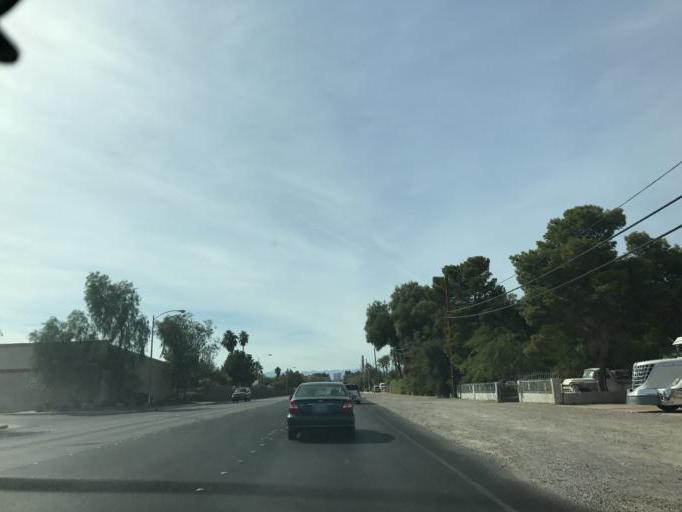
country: US
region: Nevada
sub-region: Clark County
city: Winchester
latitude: 36.1296
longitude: -115.0666
